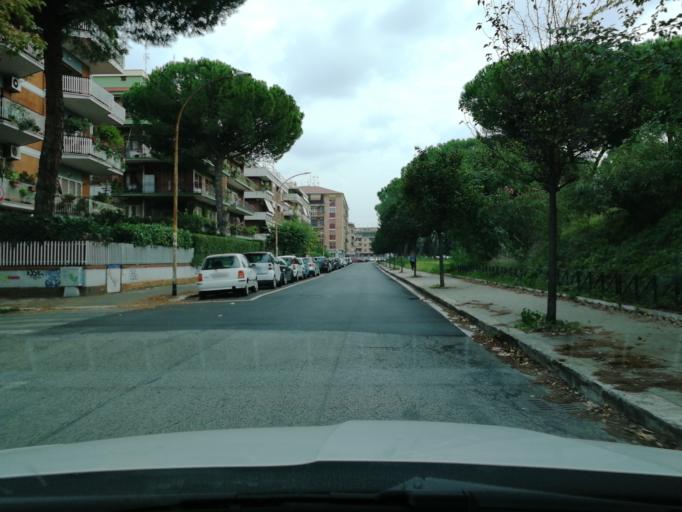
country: IT
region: Latium
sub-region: Citta metropolitana di Roma Capitale
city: Rome
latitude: 41.8545
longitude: 12.5561
